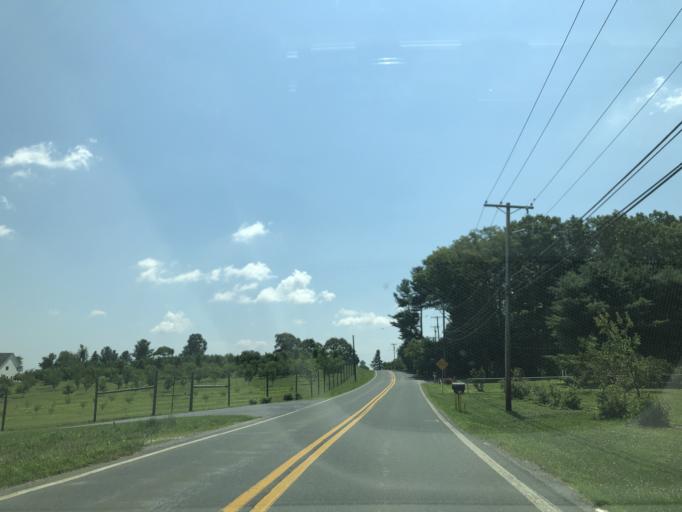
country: US
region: Maryland
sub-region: Carroll County
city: Westminster
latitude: 39.5377
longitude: -76.9725
